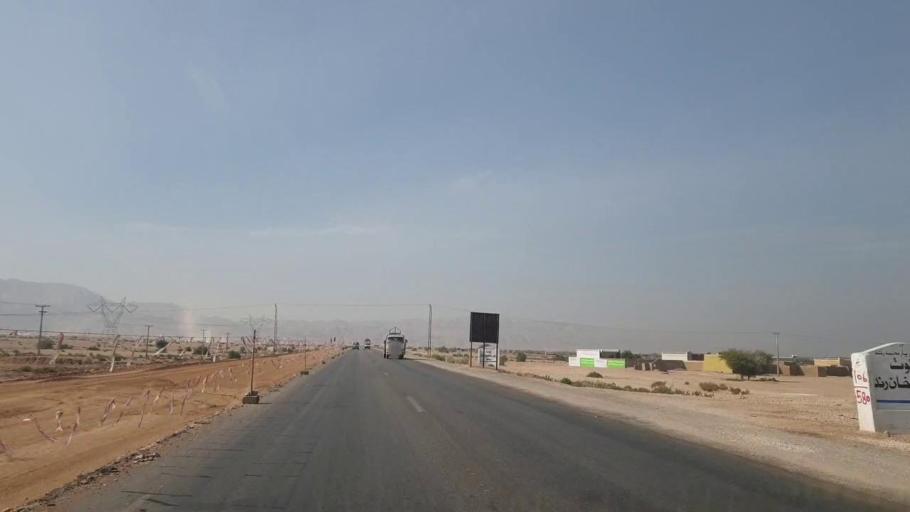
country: PK
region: Sindh
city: Sehwan
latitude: 26.2037
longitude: 67.9338
